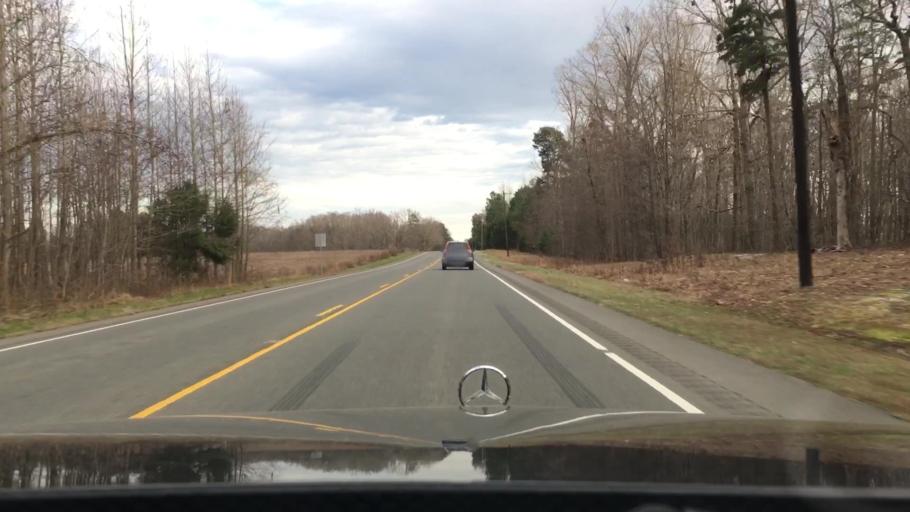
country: US
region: North Carolina
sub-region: Orange County
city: Hillsborough
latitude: 36.2117
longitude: -79.1676
